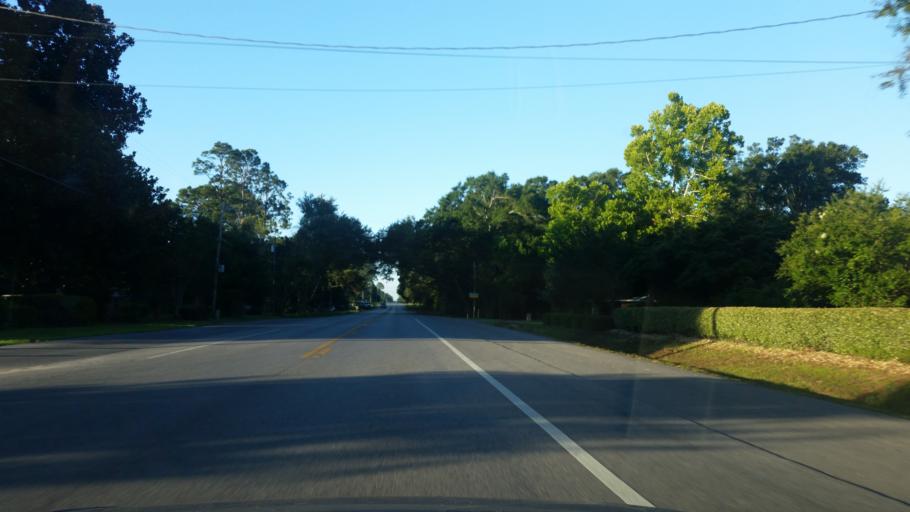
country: US
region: Florida
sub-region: Escambia County
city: Cantonment
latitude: 30.5932
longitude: -87.3492
